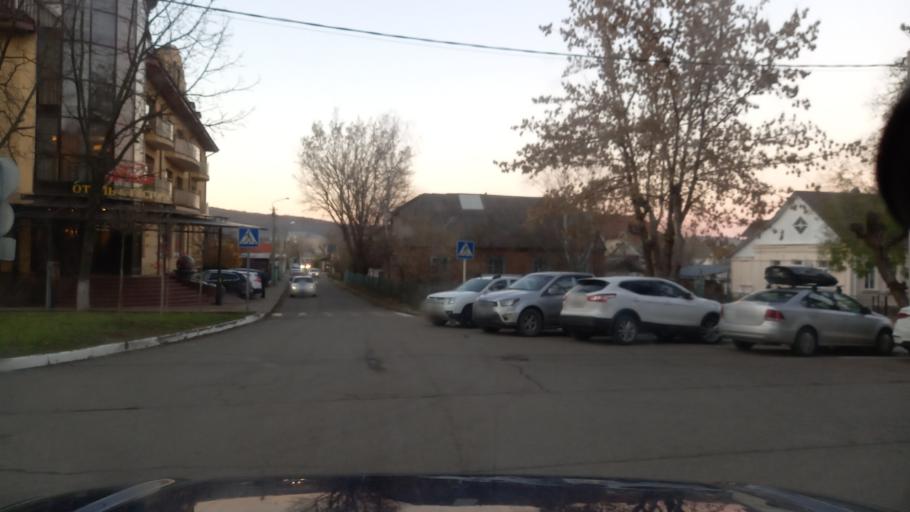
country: RU
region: Krasnodarskiy
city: Goryachiy Klyuch
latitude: 44.6260
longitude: 39.1029
